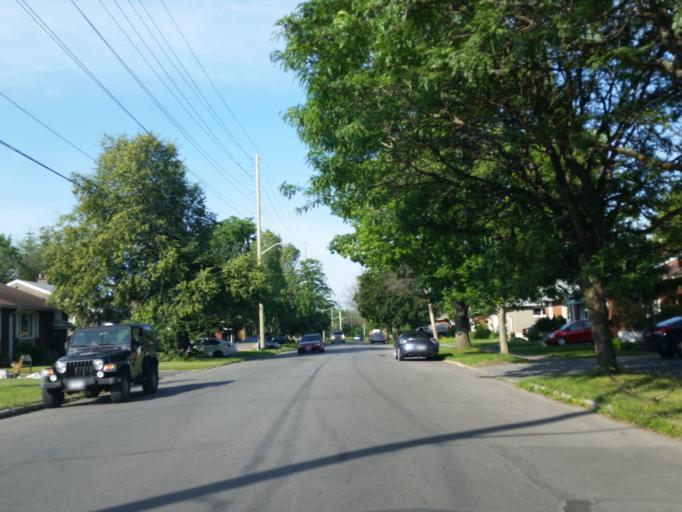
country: CA
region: Ontario
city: Bells Corners
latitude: 45.3542
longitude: -75.7724
